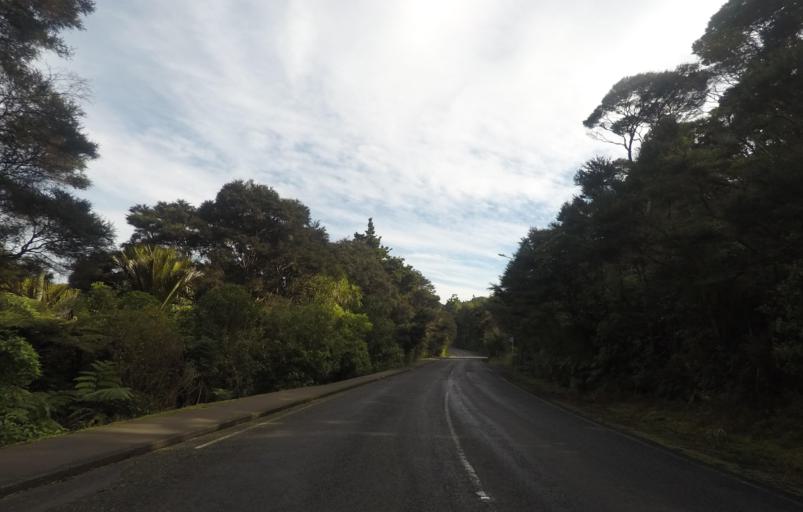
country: NZ
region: Auckland
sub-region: Auckland
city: Titirangi
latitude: -36.9378
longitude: 174.6416
